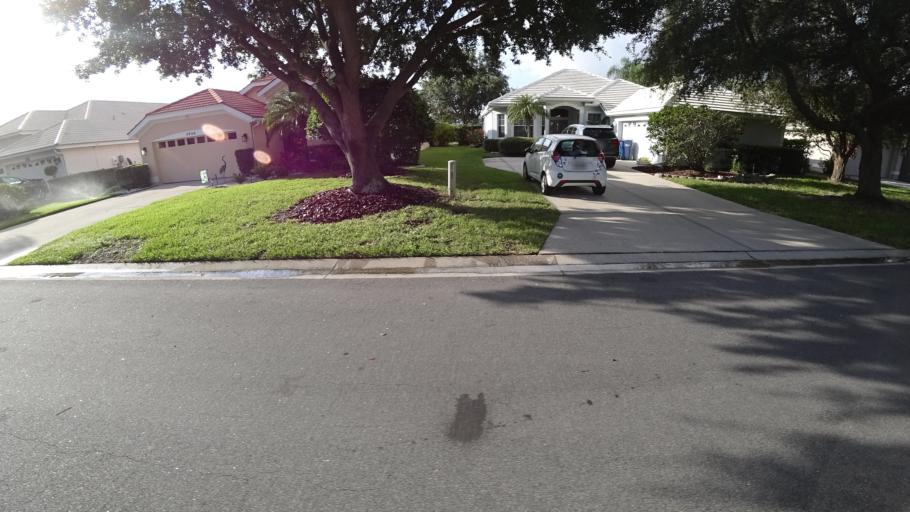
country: US
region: Florida
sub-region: Sarasota County
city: Desoto Lakes
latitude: 27.4234
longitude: -82.4846
